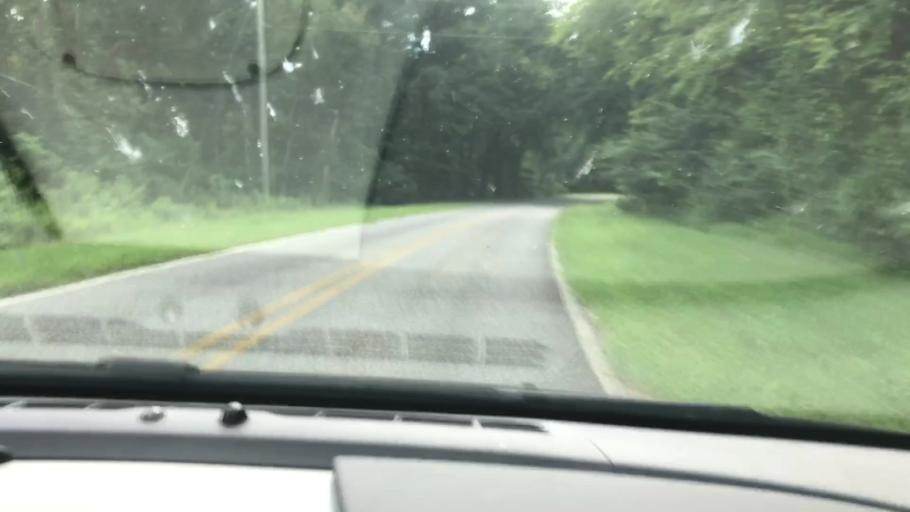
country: US
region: Georgia
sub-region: Quitman County
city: Georgetown
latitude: 31.7520
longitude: -85.0744
